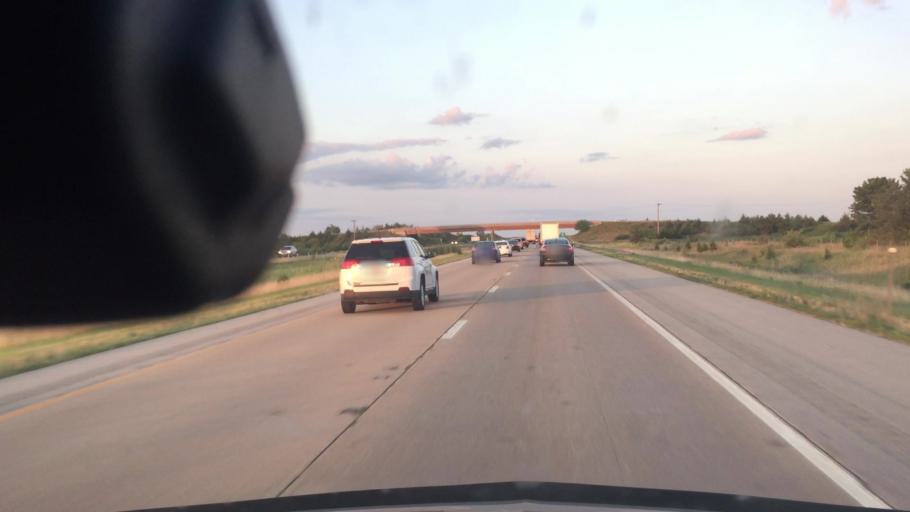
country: US
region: Illinois
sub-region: Livingston County
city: Dwight
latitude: 41.1133
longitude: -88.4368
